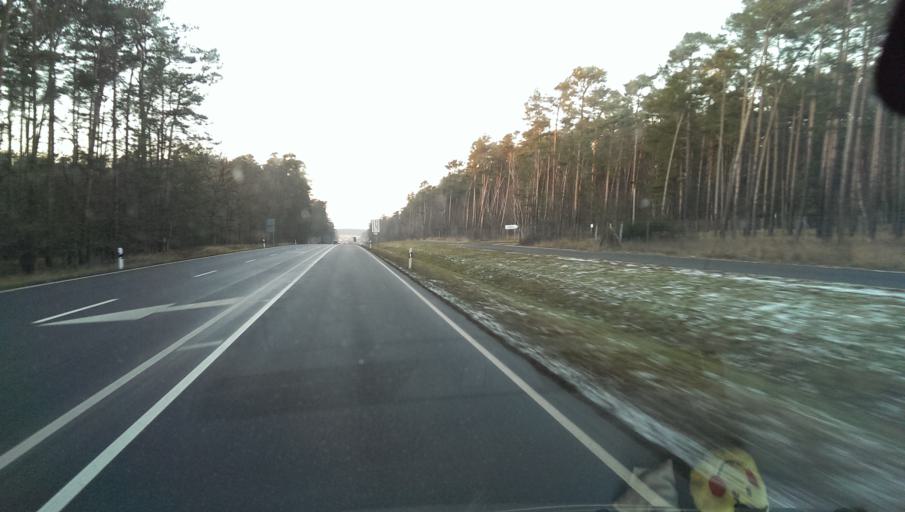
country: DE
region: Brandenburg
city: Herzberg
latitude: 51.6514
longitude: 13.2928
